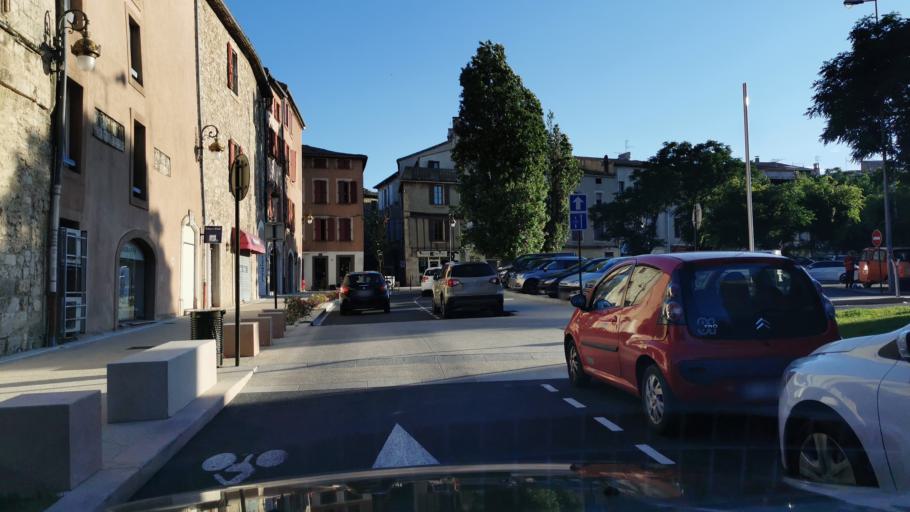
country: FR
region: Languedoc-Roussillon
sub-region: Departement de l'Aude
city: Narbonne
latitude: 43.1830
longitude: 3.0026
